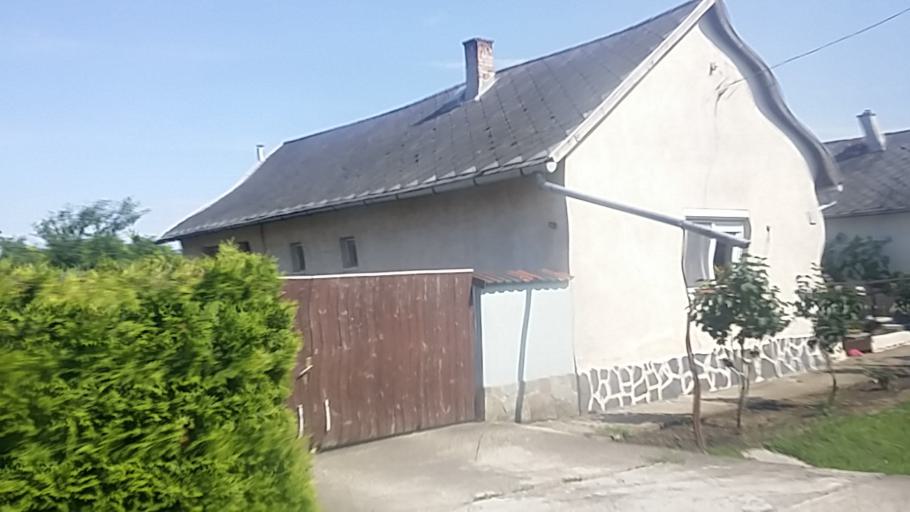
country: HU
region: Fejer
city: Ivancsa
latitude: 47.1818
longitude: 18.8273
